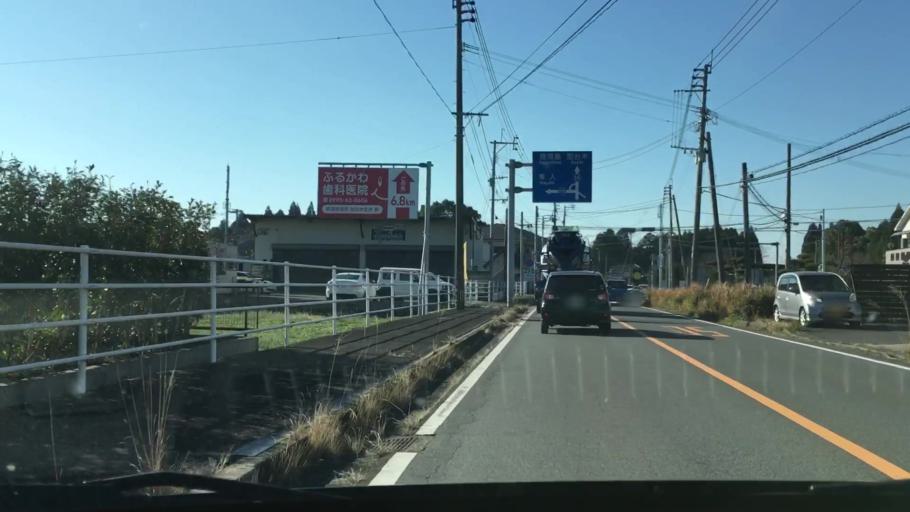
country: JP
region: Kagoshima
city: Kajiki
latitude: 31.7789
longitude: 130.7032
